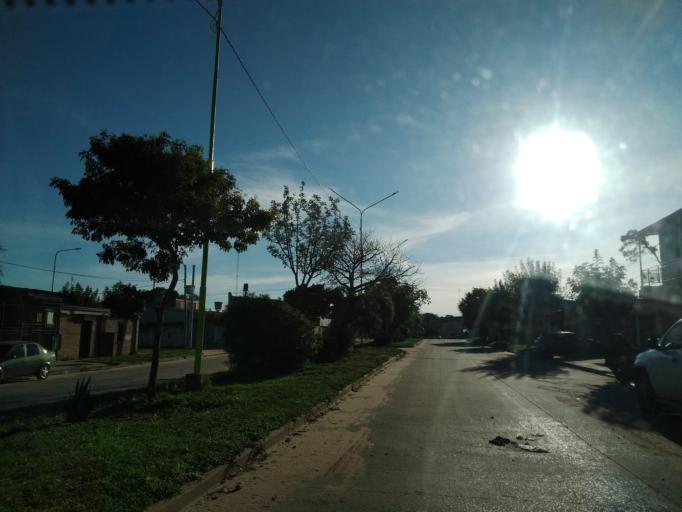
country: AR
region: Corrientes
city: Corrientes
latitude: -27.5086
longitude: -58.7958
